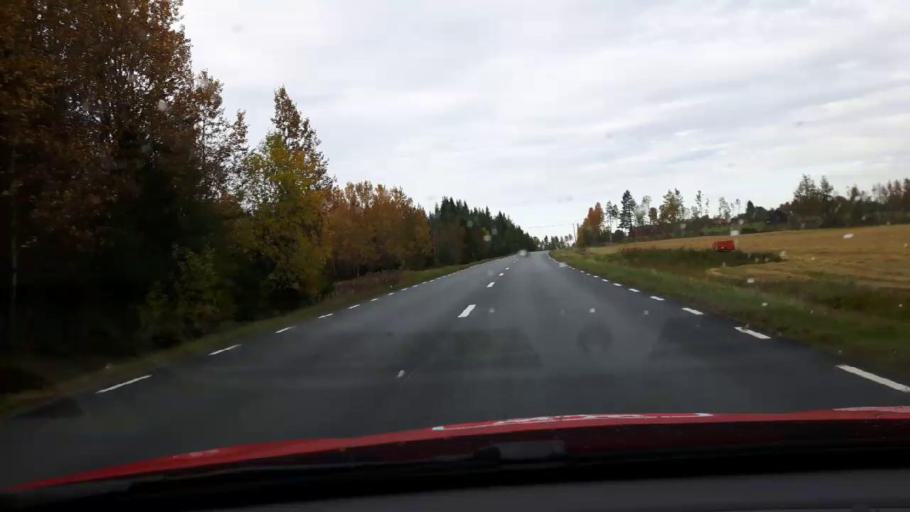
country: SE
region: Jaemtland
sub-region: Krokoms Kommun
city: Krokom
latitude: 63.1070
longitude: 14.2957
